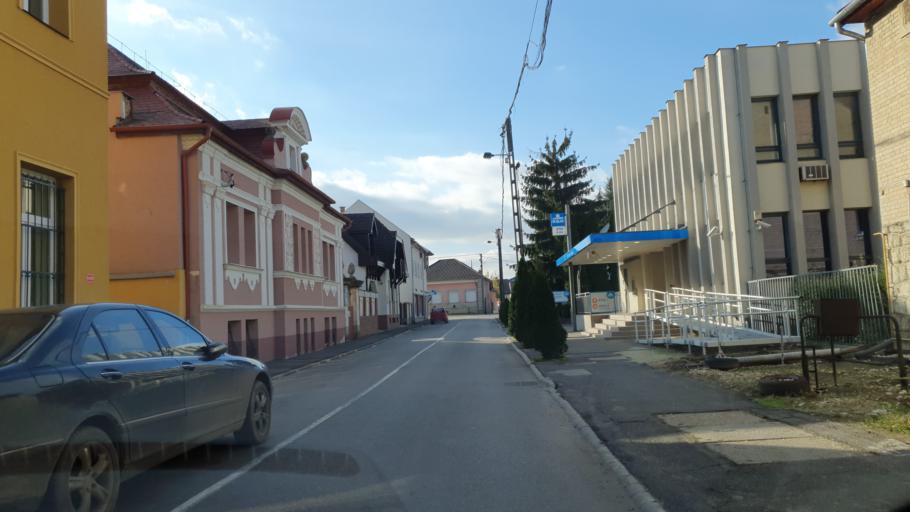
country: HU
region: Szabolcs-Szatmar-Bereg
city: Kisvarda
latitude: 48.2235
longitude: 22.0770
